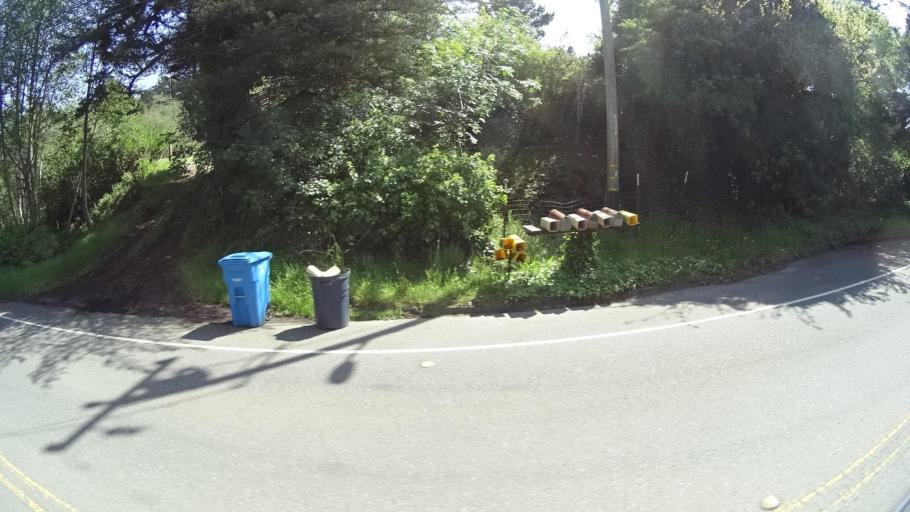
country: US
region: California
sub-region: Humboldt County
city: Hydesville
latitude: 40.5703
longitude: -124.1224
